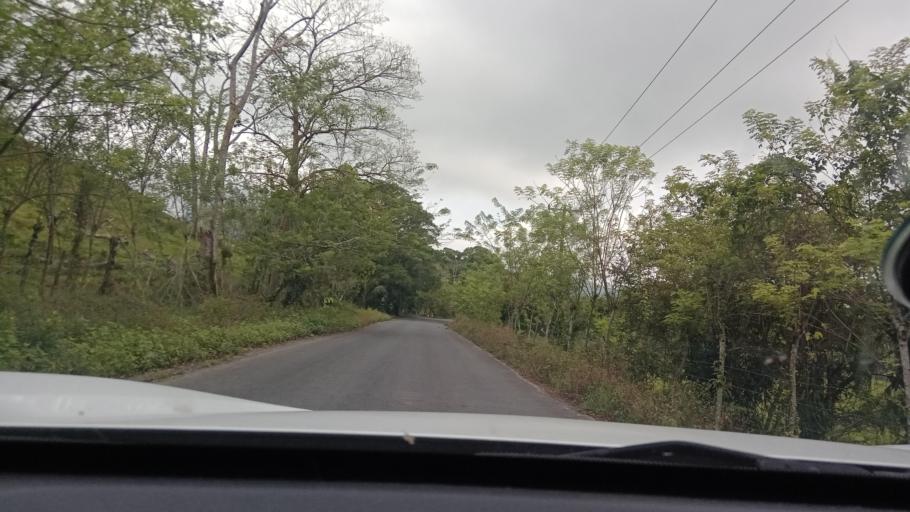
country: MX
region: Tabasco
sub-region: Huimanguillo
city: Francisco Rueda
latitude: 17.5279
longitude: -94.1250
